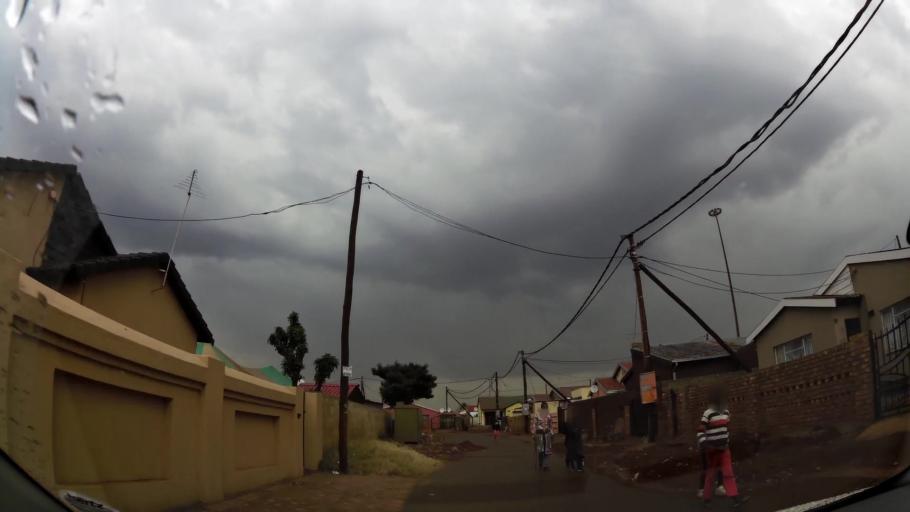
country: ZA
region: Gauteng
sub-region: Ekurhuleni Metropolitan Municipality
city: Germiston
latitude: -26.3619
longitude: 28.1376
